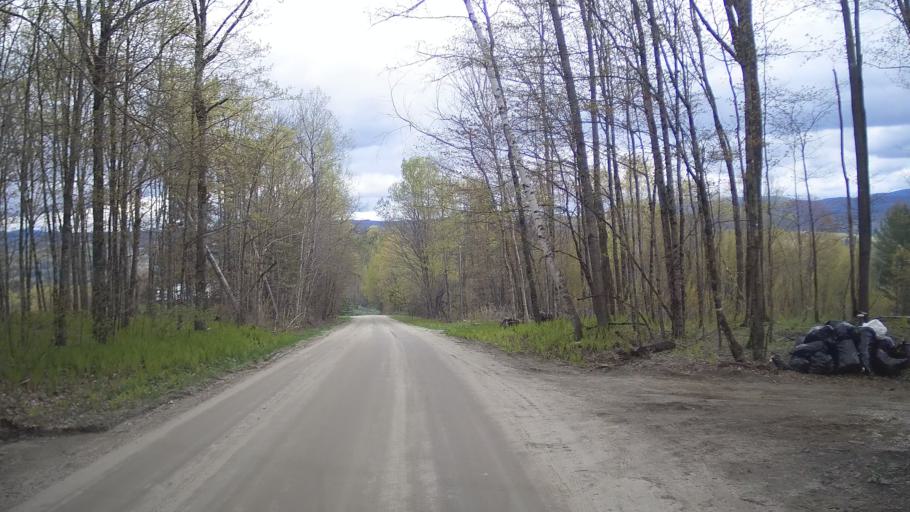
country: US
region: Vermont
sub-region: Caledonia County
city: Lyndonville
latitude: 44.5987
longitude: -71.9544
